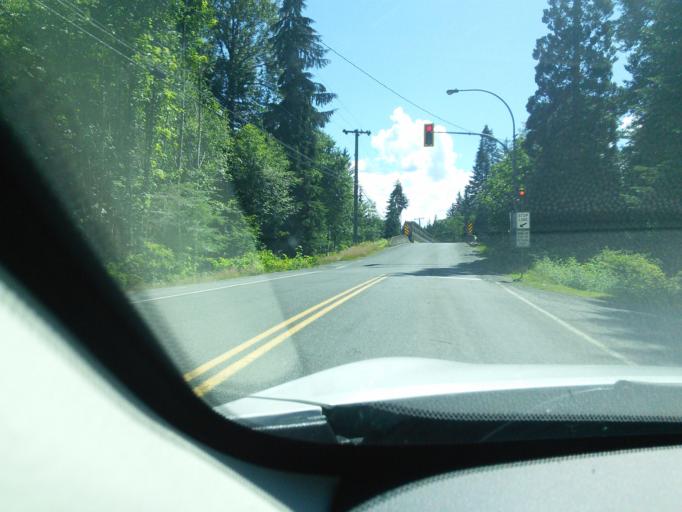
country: CA
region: British Columbia
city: Campbell River
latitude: 50.3216
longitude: -125.9221
